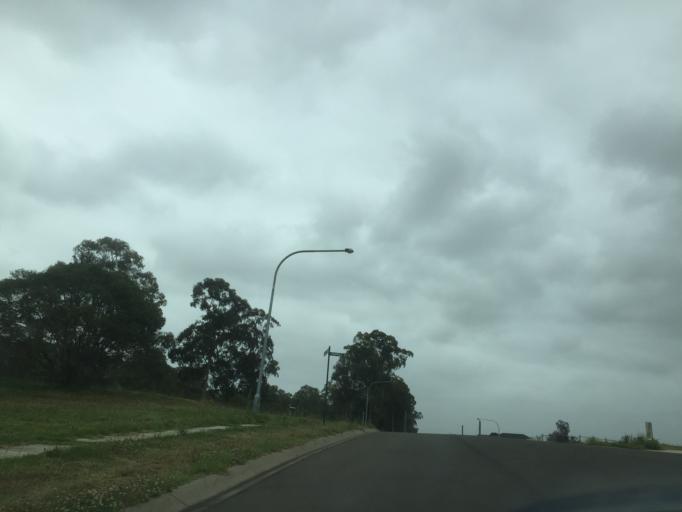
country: AU
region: New South Wales
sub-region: The Hills Shire
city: Beaumont Hills
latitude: -33.7220
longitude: 150.9519
